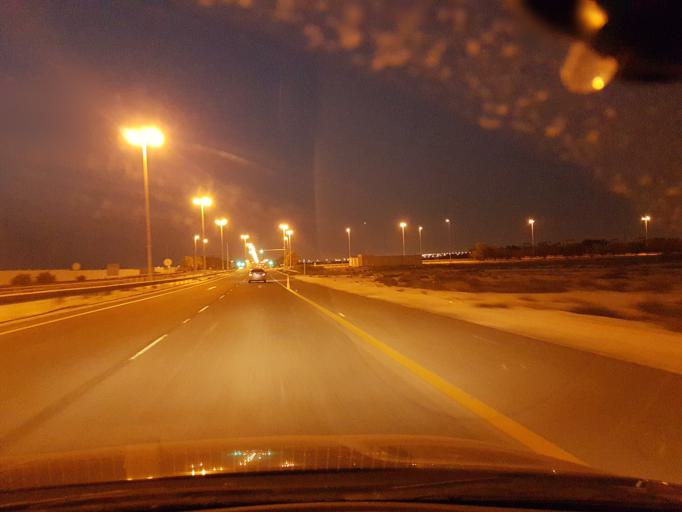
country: BH
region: Central Governorate
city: Dar Kulayb
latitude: 26.0362
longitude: 50.5000
